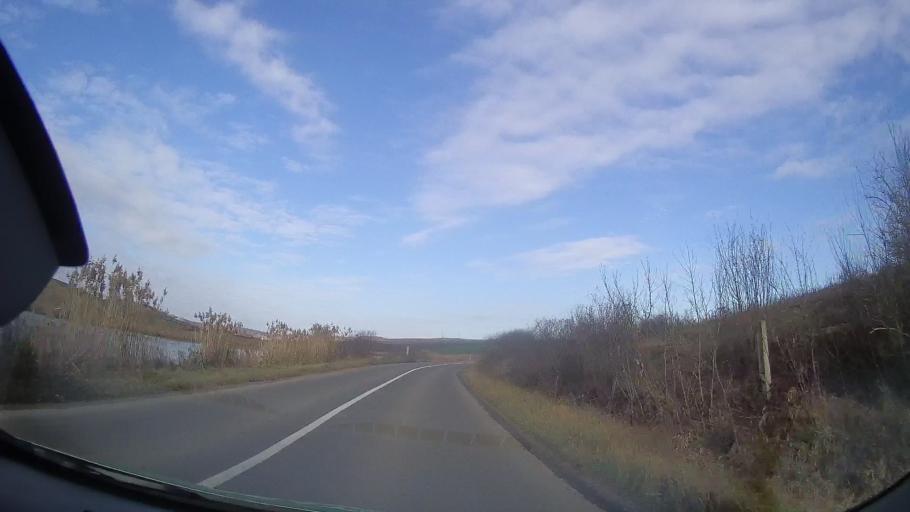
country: RO
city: Barza
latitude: 46.5583
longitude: 24.0987
